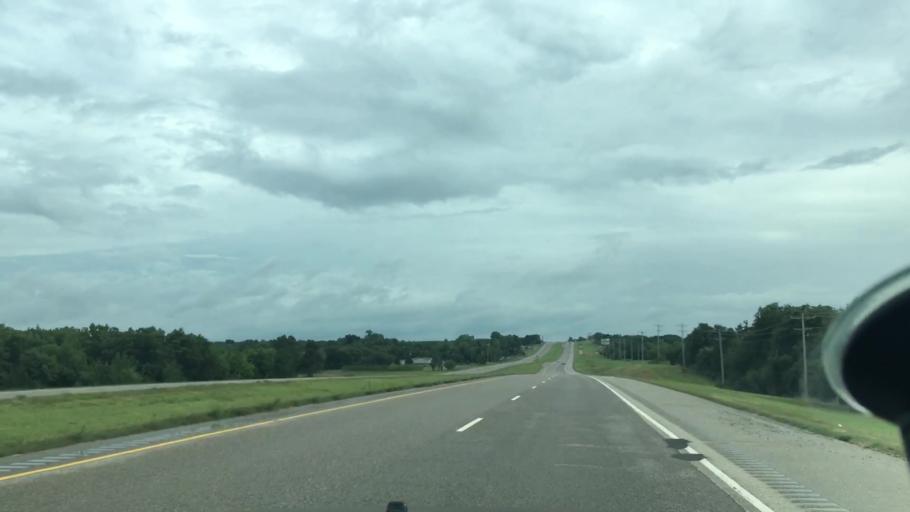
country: US
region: Oklahoma
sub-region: Seminole County
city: Seminole
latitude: 35.3311
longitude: -96.6716
